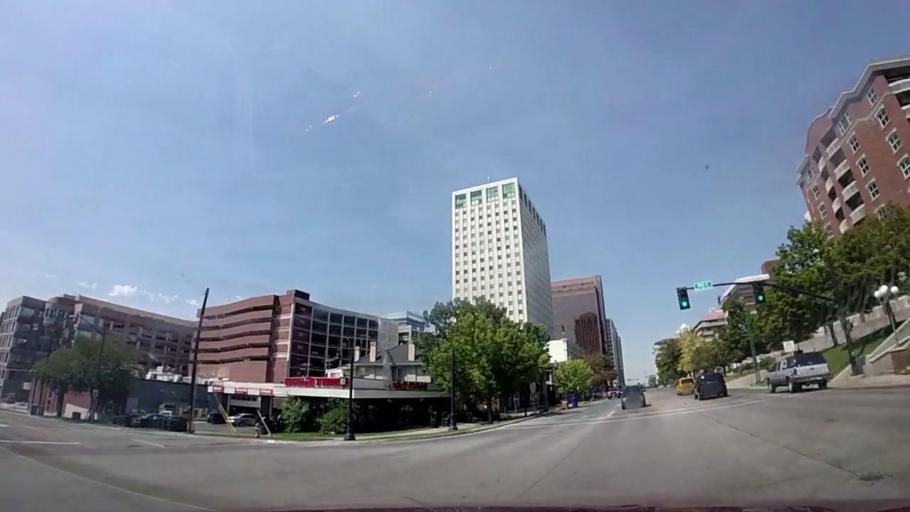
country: US
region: Utah
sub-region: Salt Lake County
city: Salt Lake City
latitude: 40.7692
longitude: -111.8853
